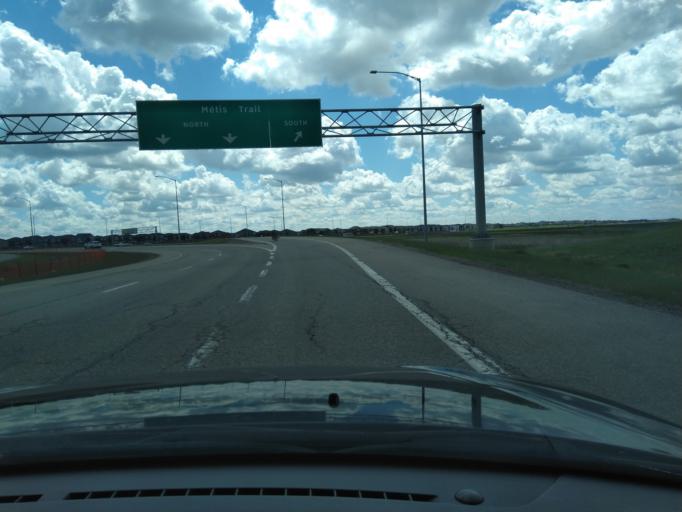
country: CA
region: Alberta
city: Airdrie
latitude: 51.1740
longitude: -113.9726
